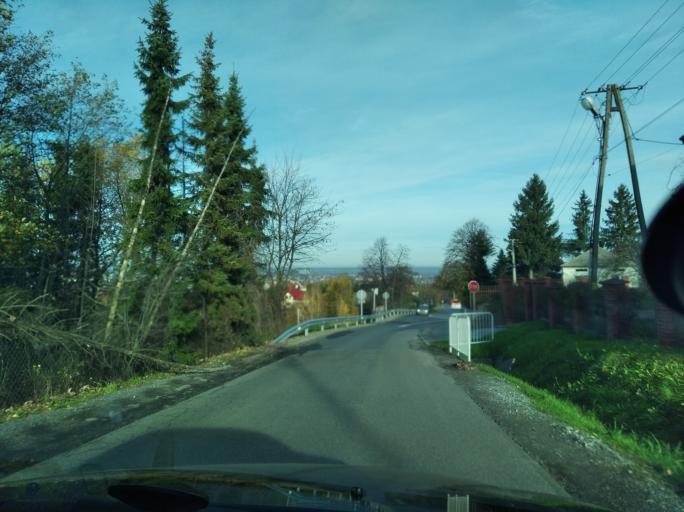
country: PL
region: Subcarpathian Voivodeship
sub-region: Powiat rzeszowski
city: Tyczyn
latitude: 50.0045
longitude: 22.0682
